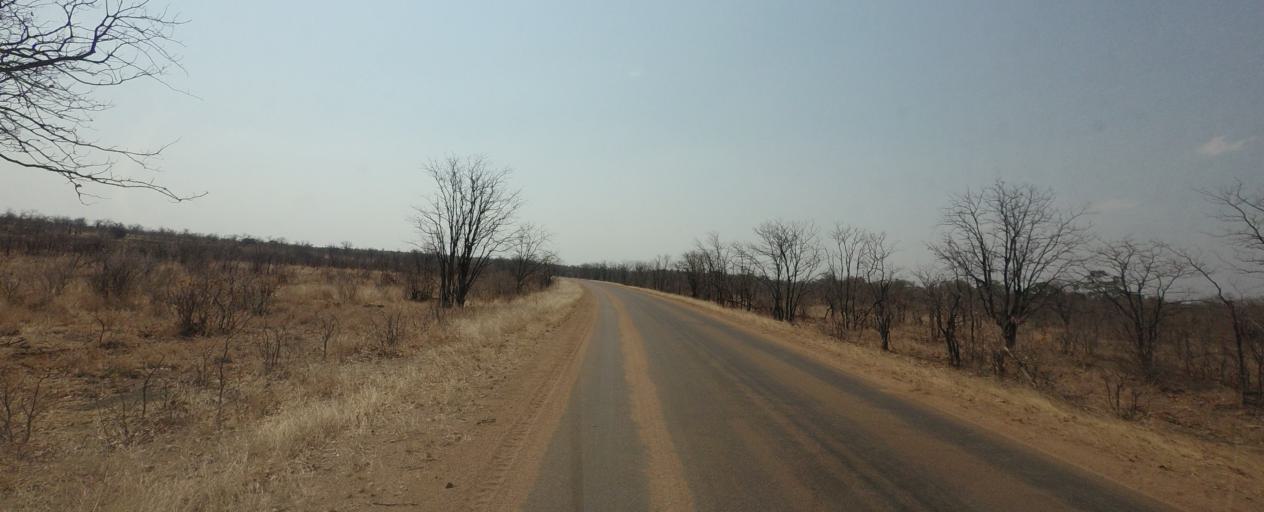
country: ZA
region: Limpopo
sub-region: Mopani District Municipality
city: Giyani
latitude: -23.2119
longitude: 31.3152
